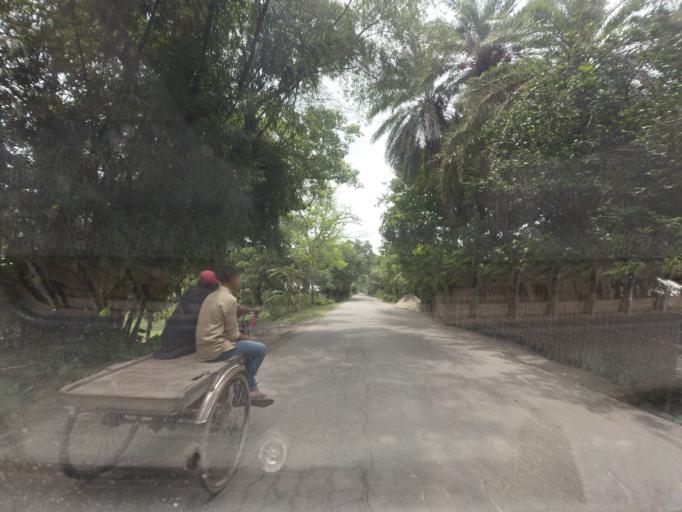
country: BD
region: Khulna
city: Kalia
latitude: 23.2091
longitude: 89.7055
